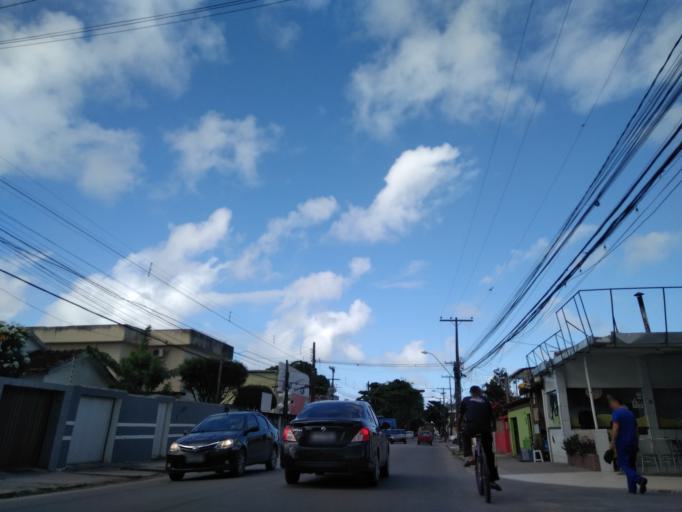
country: BR
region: Pernambuco
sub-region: Recife
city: Recife
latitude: -8.0754
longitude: -34.9172
